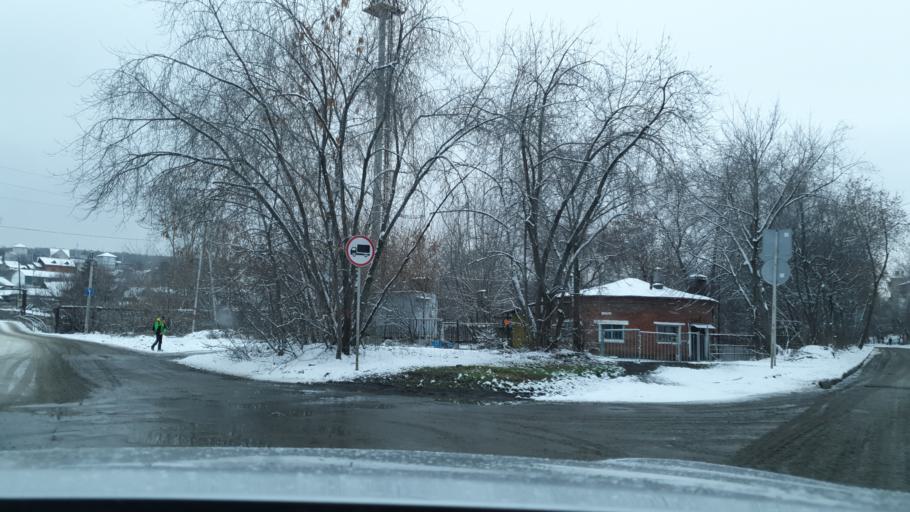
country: RU
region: Sverdlovsk
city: Istok
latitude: 56.7495
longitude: 60.7004
